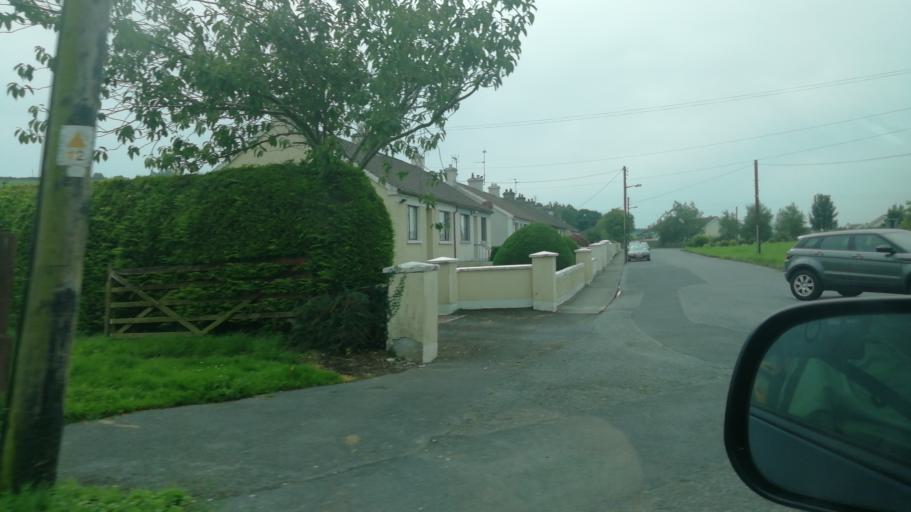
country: IE
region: Munster
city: Fethard
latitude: 52.5700
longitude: -7.6662
